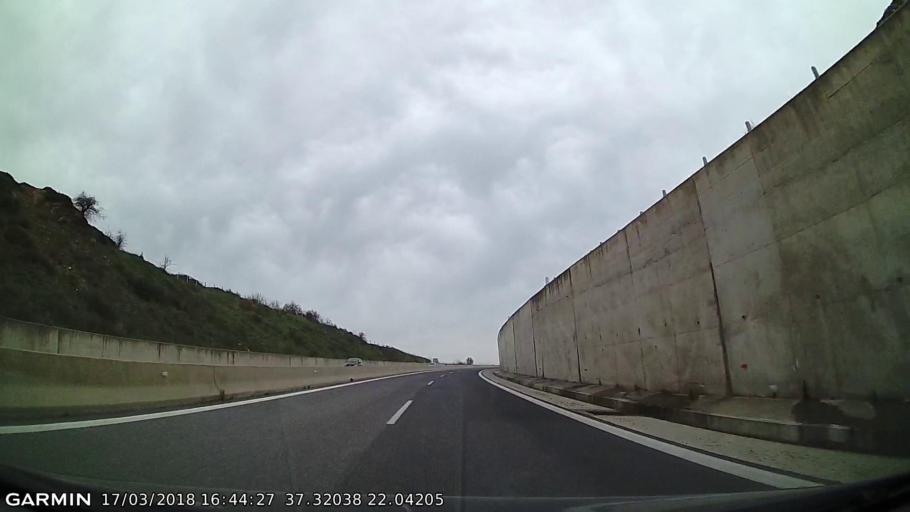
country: GR
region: Peloponnese
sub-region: Nomos Arkadias
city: Megalopoli
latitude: 37.3216
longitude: 22.0428
